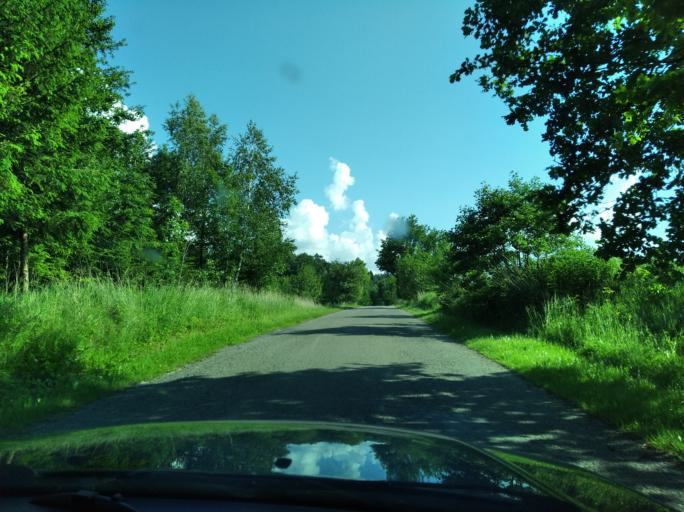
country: PL
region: Subcarpathian Voivodeship
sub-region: Powiat jaroslawski
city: Kramarzowka
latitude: 49.8613
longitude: 22.5159
